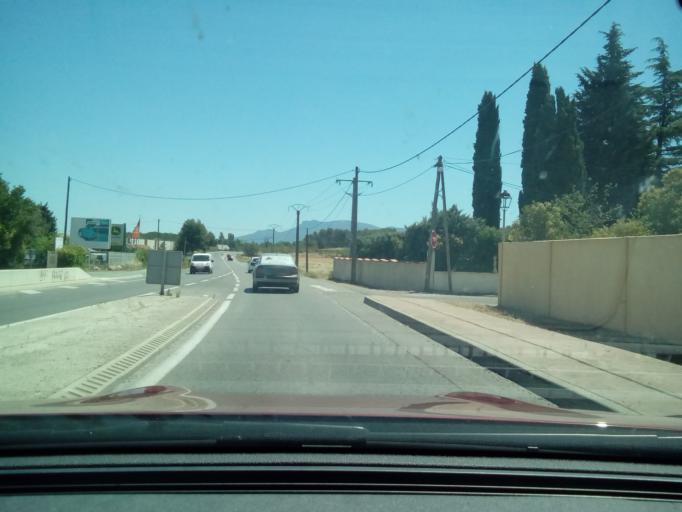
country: FR
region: Provence-Alpes-Cote d'Azur
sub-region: Departement des Bouches-du-Rhone
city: Rousset
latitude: 43.4628
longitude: 5.6134
